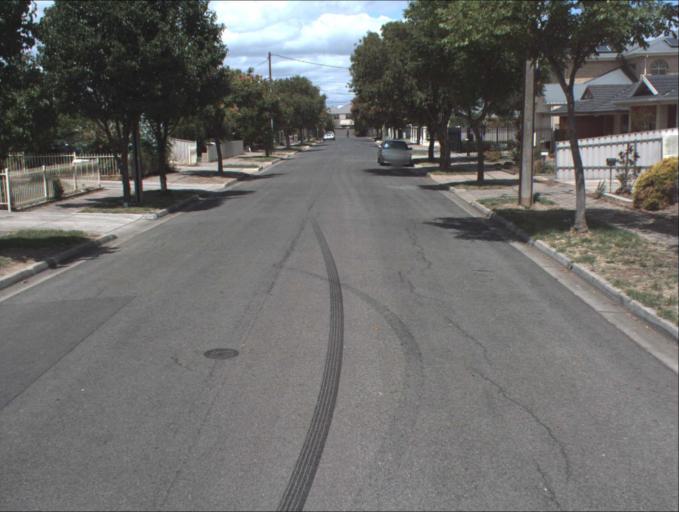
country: AU
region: South Australia
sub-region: Port Adelaide Enfield
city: Enfield
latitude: -34.8568
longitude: 138.6259
